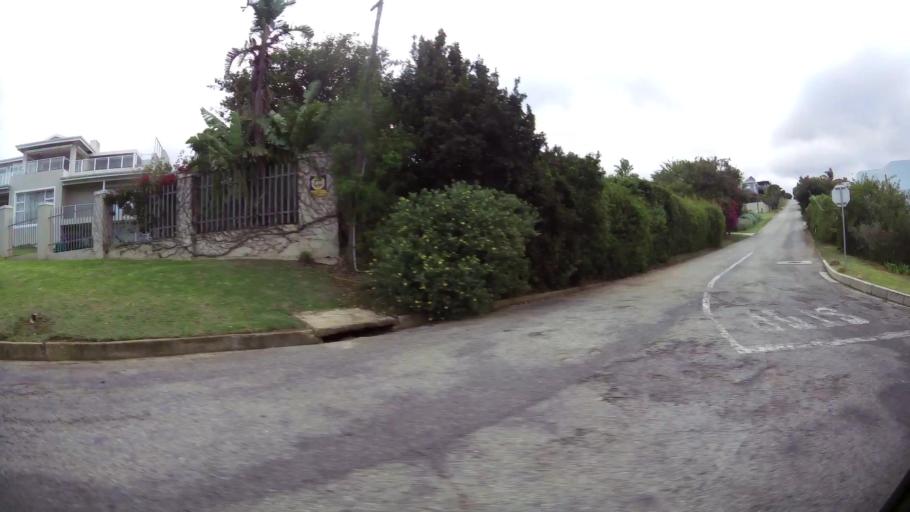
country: ZA
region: Western Cape
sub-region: Eden District Municipality
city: Plettenberg Bay
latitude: -34.0586
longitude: 23.3742
